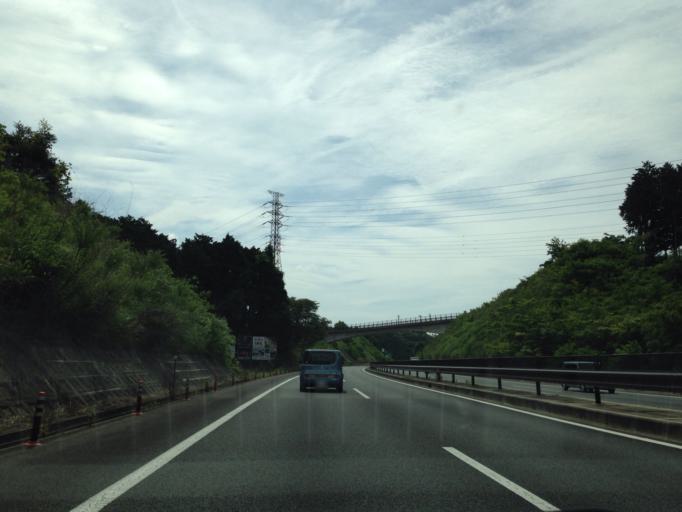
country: JP
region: Shizuoka
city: Mishima
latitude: 35.1505
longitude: 138.9304
